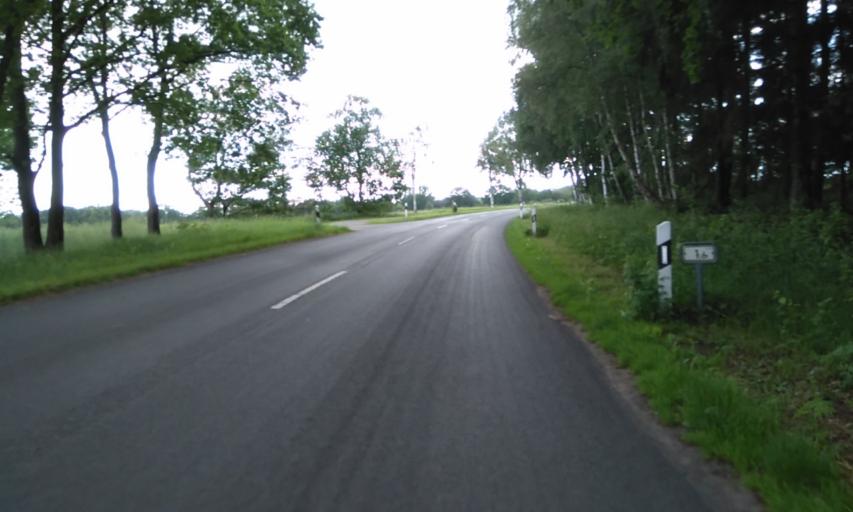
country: DE
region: Lower Saxony
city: Wohnste
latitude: 53.3581
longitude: 9.5524
